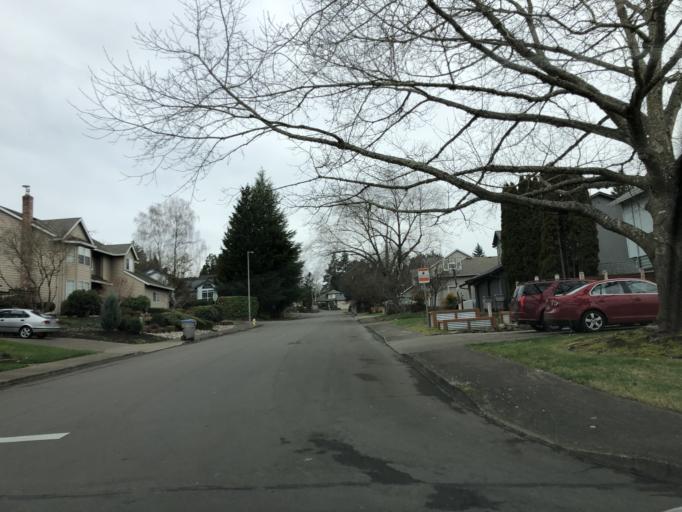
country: US
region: Oregon
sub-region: Washington County
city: Tigard
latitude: 45.4179
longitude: -122.7763
